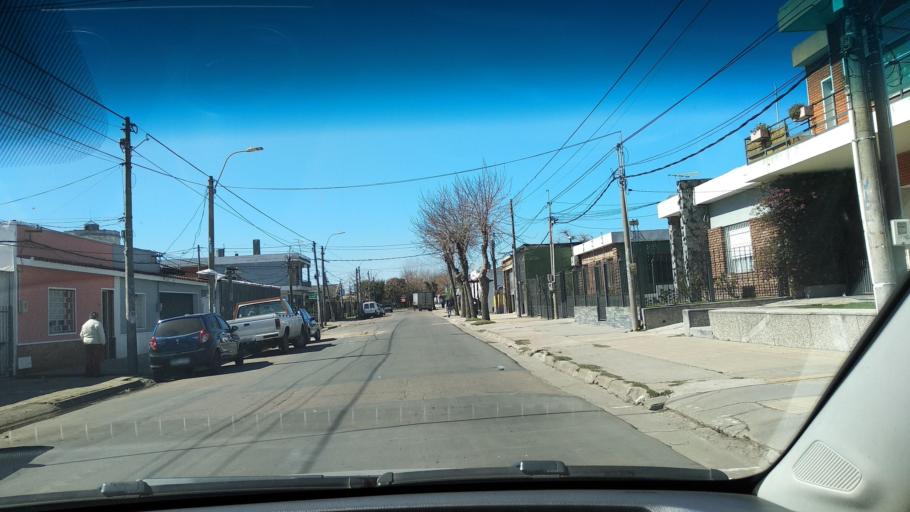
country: UY
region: Canelones
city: Las Piedras
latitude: -34.7260
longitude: -56.2121
